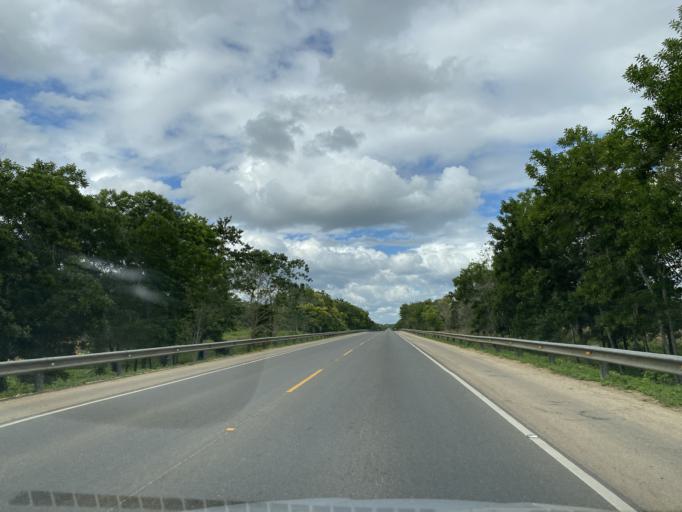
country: DO
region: Santo Domingo
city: Guerra
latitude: 18.5353
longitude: -69.7546
